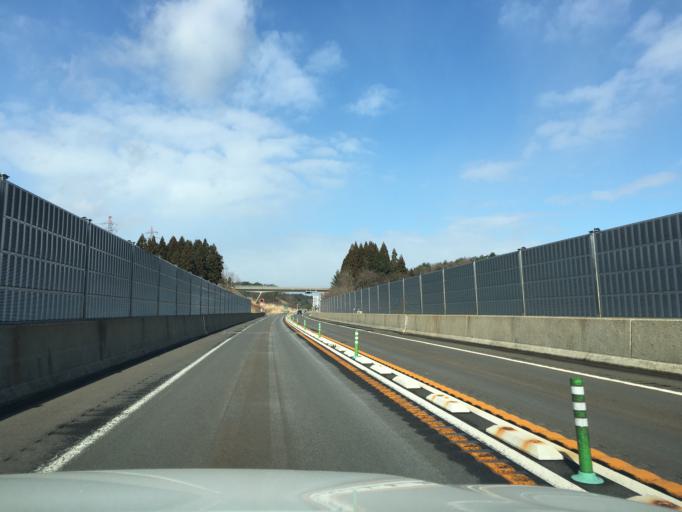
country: JP
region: Akita
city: Akita
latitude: 39.7562
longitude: 140.1369
